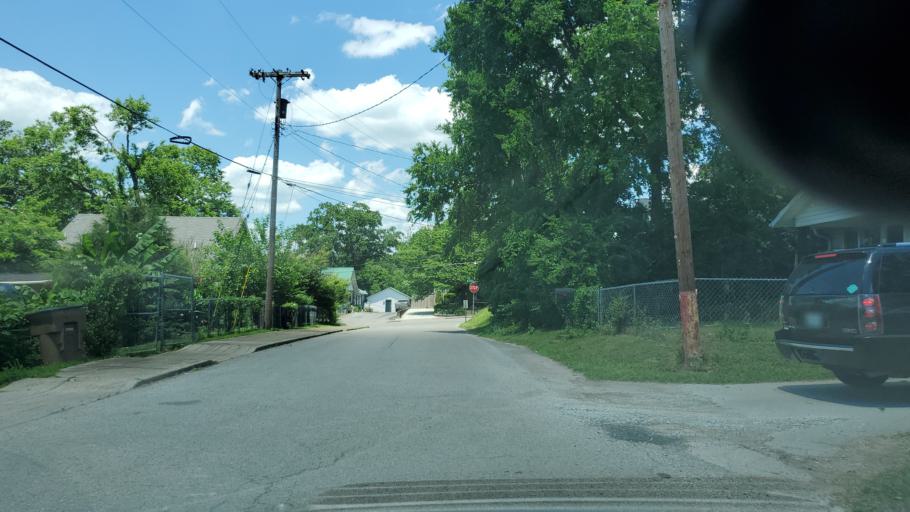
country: US
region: Tennessee
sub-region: Davidson County
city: Nashville
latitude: 36.1902
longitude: -86.7501
